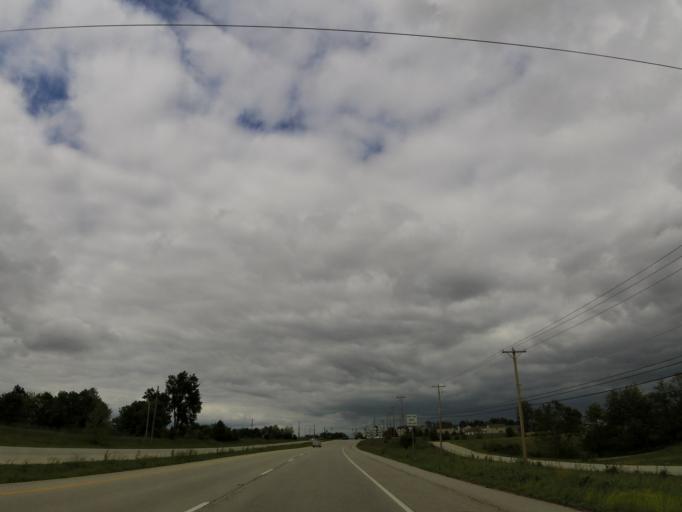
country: US
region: Kentucky
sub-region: Scott County
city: Georgetown
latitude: 38.1947
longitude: -84.5865
